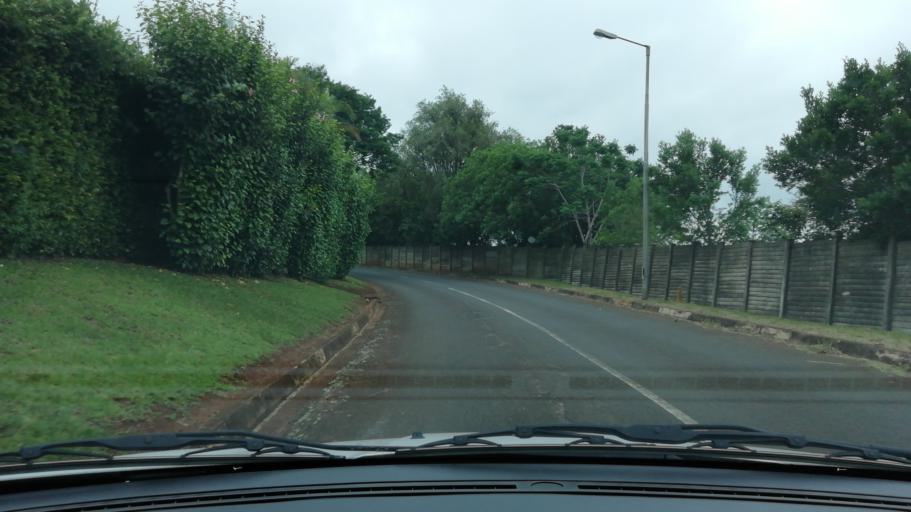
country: ZA
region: KwaZulu-Natal
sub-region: uThungulu District Municipality
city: Empangeni
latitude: -28.7474
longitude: 31.8962
